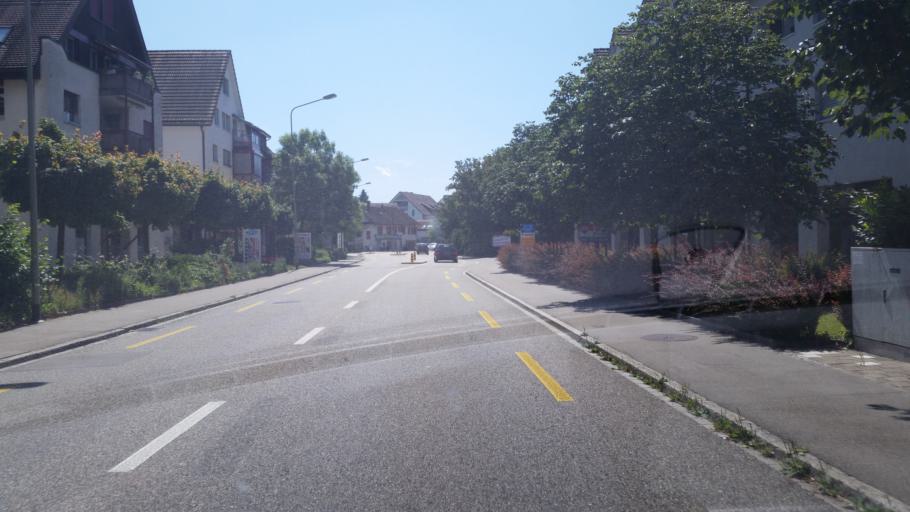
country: CH
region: Zurich
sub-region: Bezirk Buelach
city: Bulach
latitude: 47.5191
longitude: 8.5420
